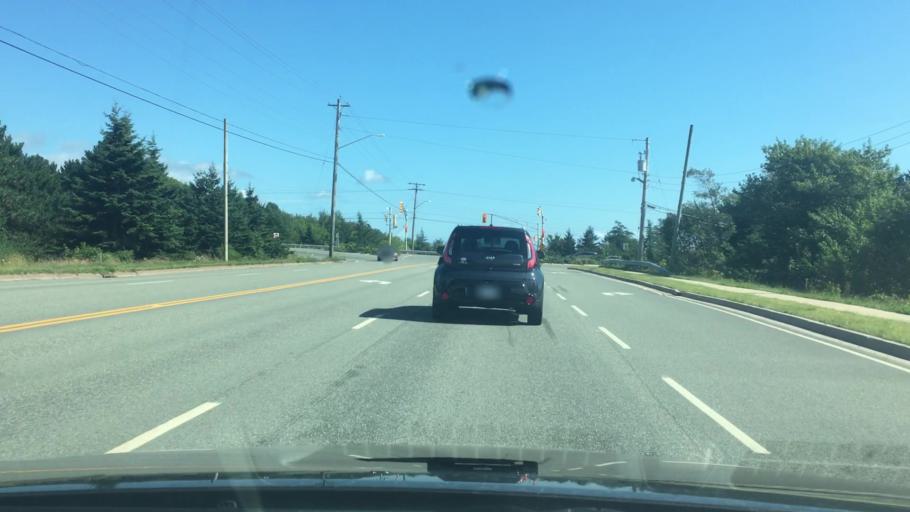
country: CA
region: Nova Scotia
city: Port Hawkesbury
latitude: 45.6126
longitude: -61.3462
